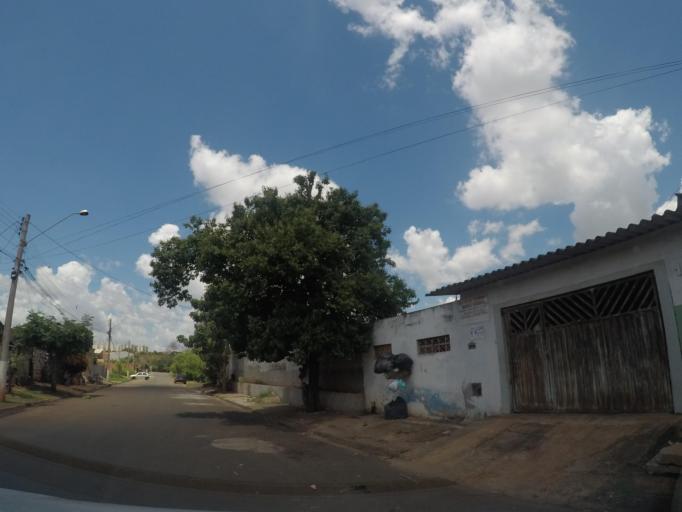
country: BR
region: Sao Paulo
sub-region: Hortolandia
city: Hortolandia
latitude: -22.8232
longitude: -47.2007
